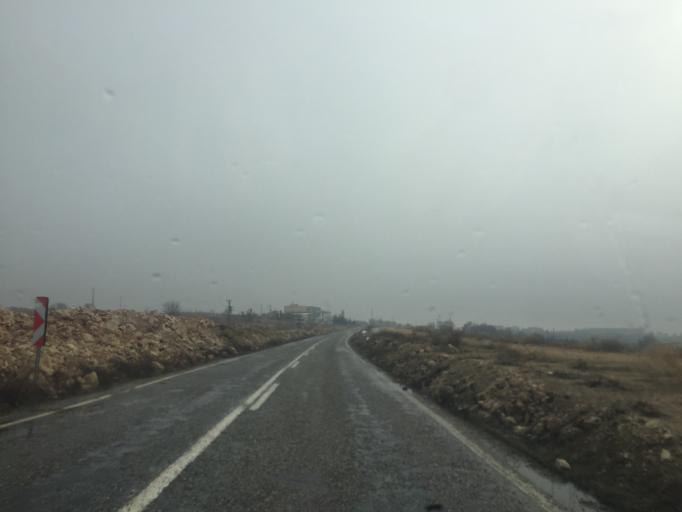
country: TR
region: Mardin
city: Omerli
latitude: 37.3959
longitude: 40.9242
